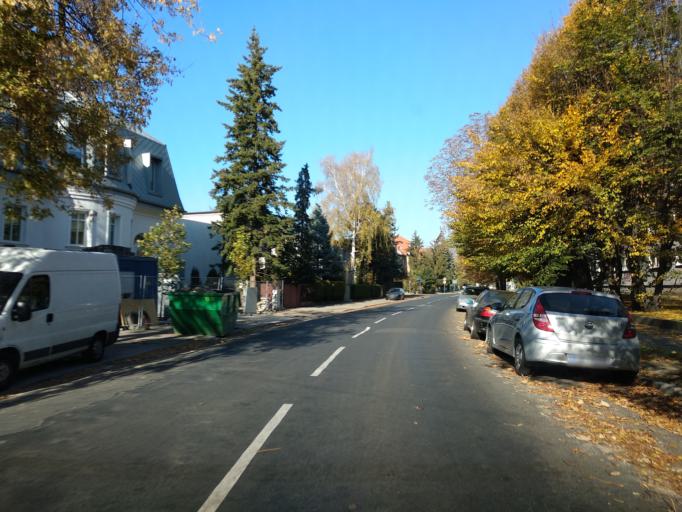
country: PL
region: Lower Silesian Voivodeship
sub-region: Powiat wroclawski
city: Wroclaw
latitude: 51.0829
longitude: 17.0027
